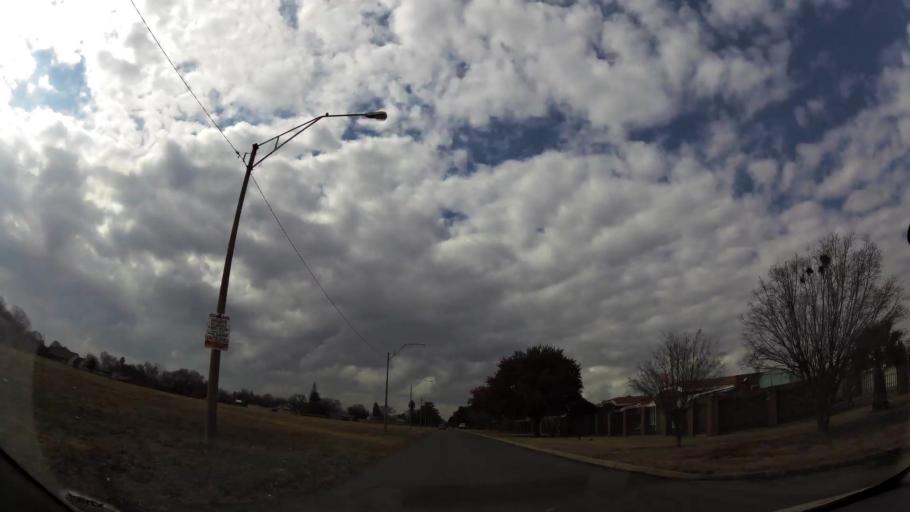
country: ZA
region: Gauteng
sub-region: Sedibeng District Municipality
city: Vereeniging
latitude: -26.6541
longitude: 27.9865
